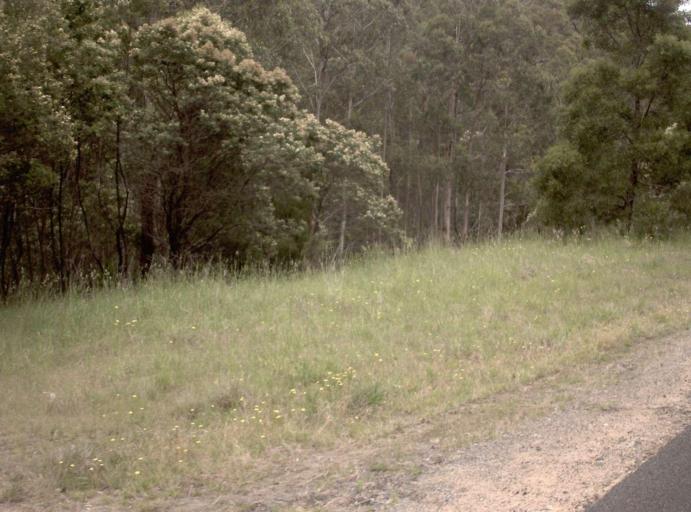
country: AU
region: New South Wales
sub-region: Bombala
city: Bombala
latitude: -37.2391
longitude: 149.2642
